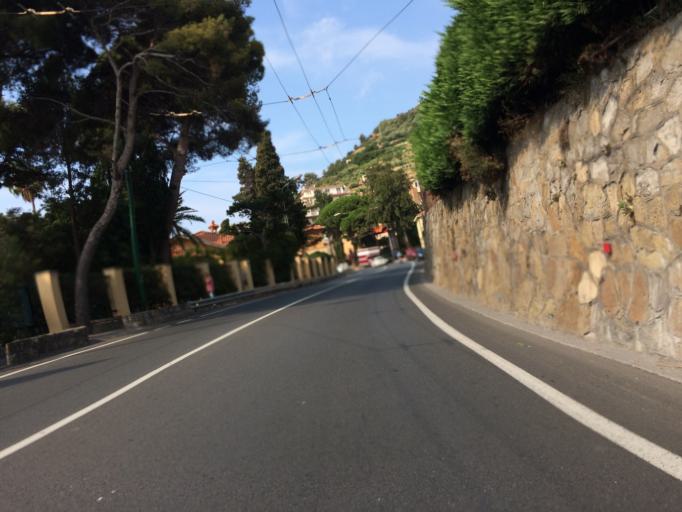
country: IT
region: Liguria
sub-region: Provincia di Imperia
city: Ospedaletti
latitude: 43.8010
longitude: 7.7433
